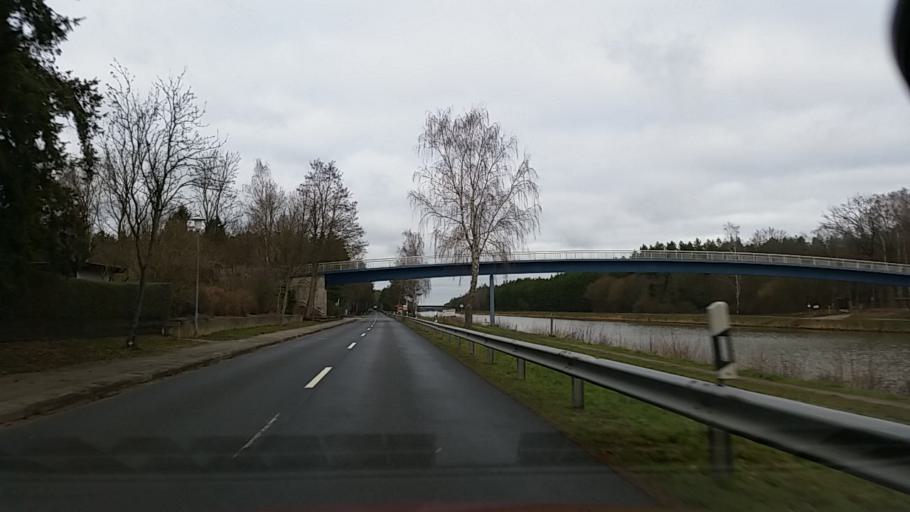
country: DE
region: Lower Saxony
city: Bodenteich
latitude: 52.8387
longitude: 10.6658
